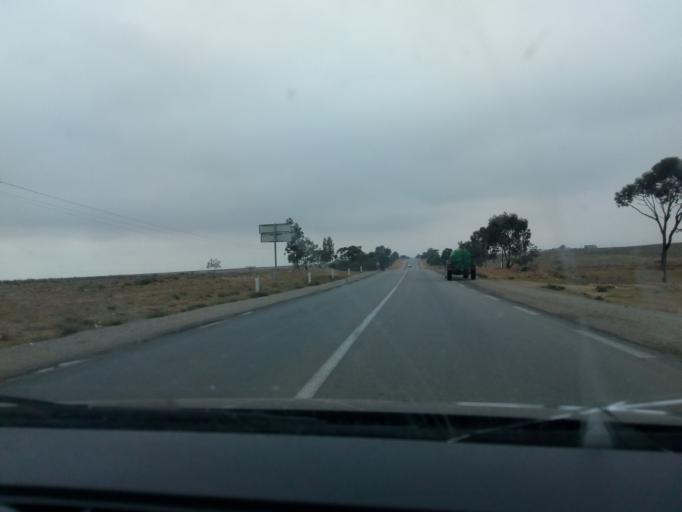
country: TN
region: Madanin
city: Medenine
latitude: 33.2709
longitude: 10.4678
